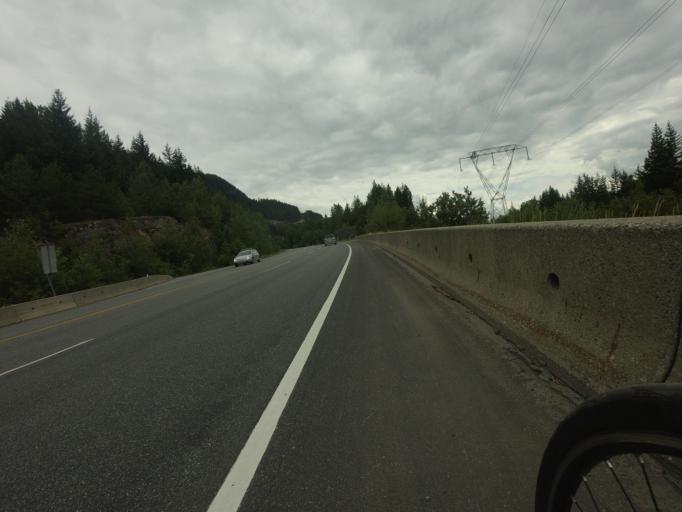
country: CA
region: British Columbia
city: Whistler
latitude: 49.8573
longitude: -123.1556
